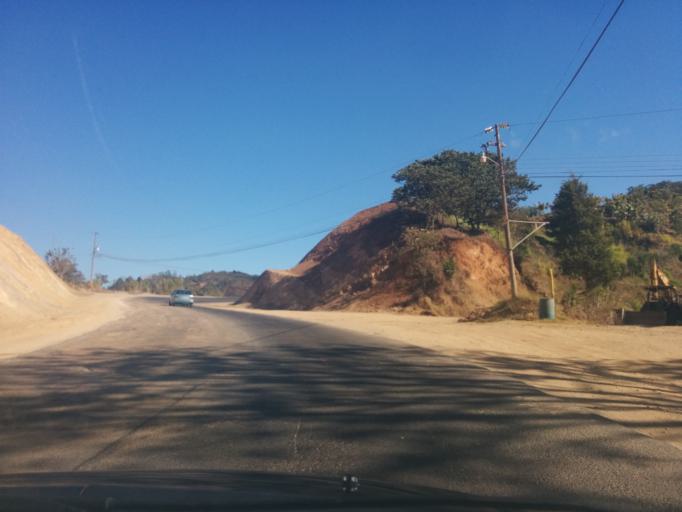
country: CR
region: Alajuela
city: San Rafael
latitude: 10.0386
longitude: -84.5052
